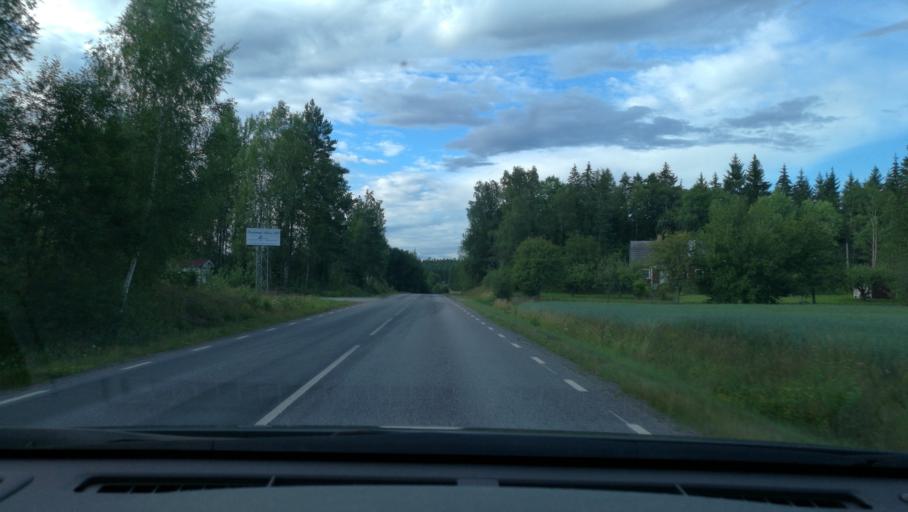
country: SE
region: OEstergoetland
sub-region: Norrkopings Kommun
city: Svartinge
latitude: 58.7207
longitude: 15.9422
